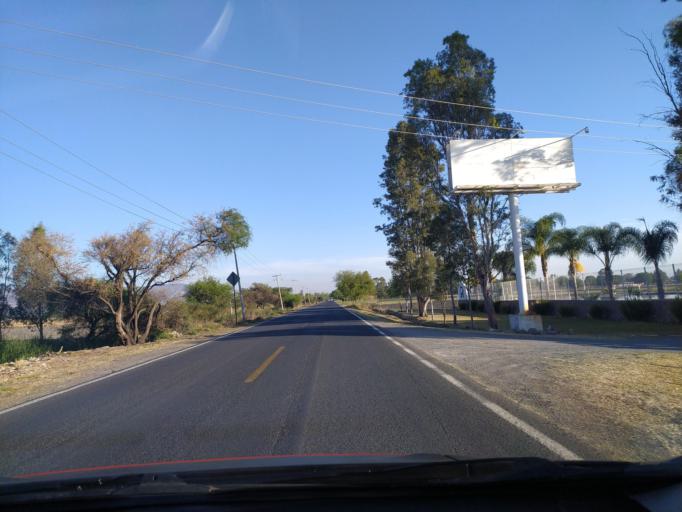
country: MX
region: Guanajuato
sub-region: San Francisco del Rincon
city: San Ignacio de Hidalgo
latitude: 20.9379
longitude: -101.8545
